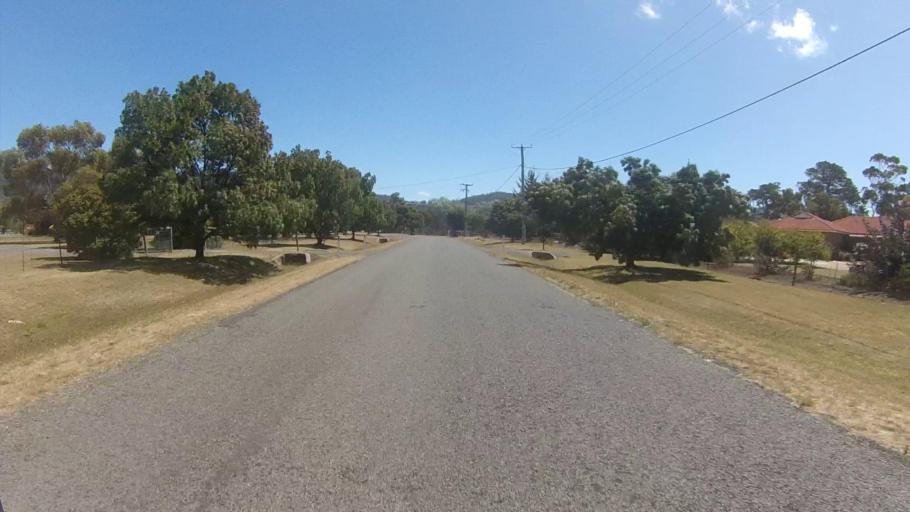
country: AU
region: Tasmania
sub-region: Clarence
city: Cambridge
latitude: -42.8428
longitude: 147.4759
